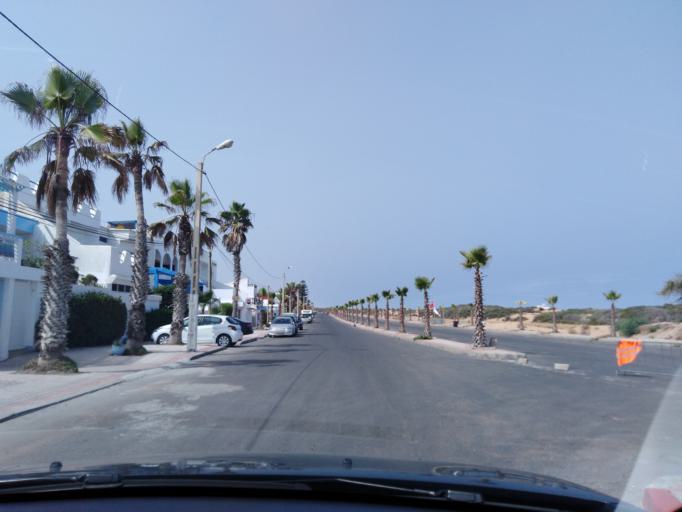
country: MA
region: Doukkala-Abda
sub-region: Safi
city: Safi
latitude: 32.7314
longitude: -9.0467
